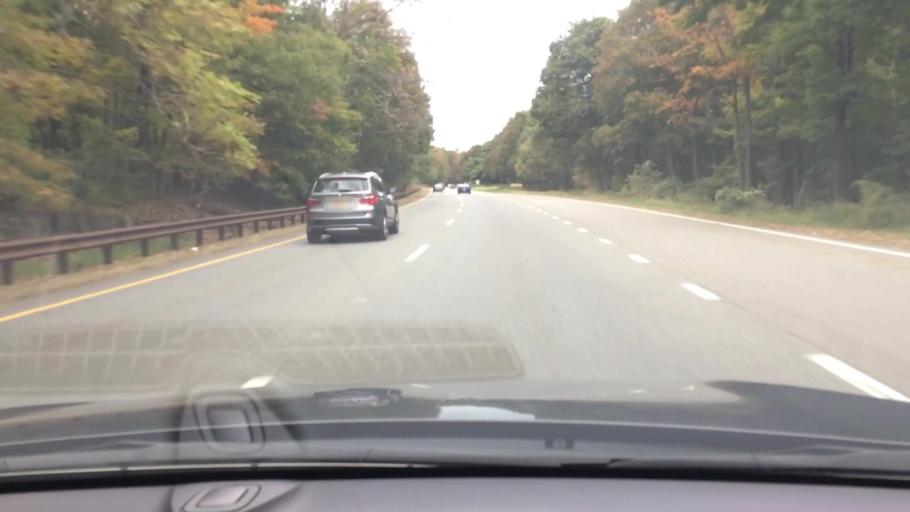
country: US
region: New Jersey
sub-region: Bergen County
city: Alpine
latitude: 40.9592
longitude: -73.9186
